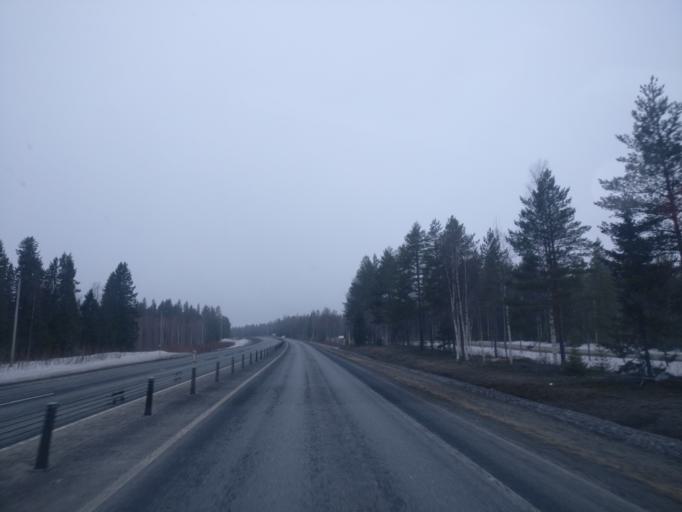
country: FI
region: Lapland
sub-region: Kemi-Tornio
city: Simo
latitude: 65.6679
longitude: 24.9707
